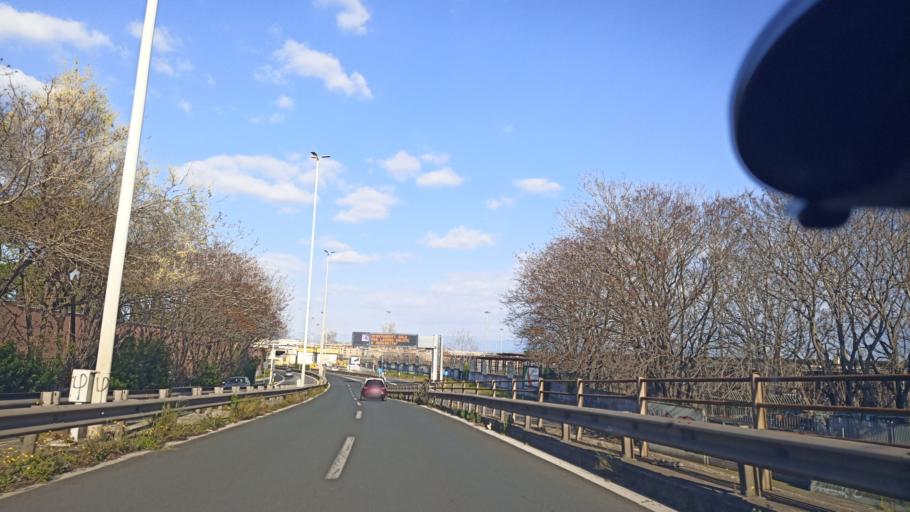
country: IT
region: Latium
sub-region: Citta metropolitana di Roma Capitale
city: Rome
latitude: 41.8972
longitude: 12.5226
